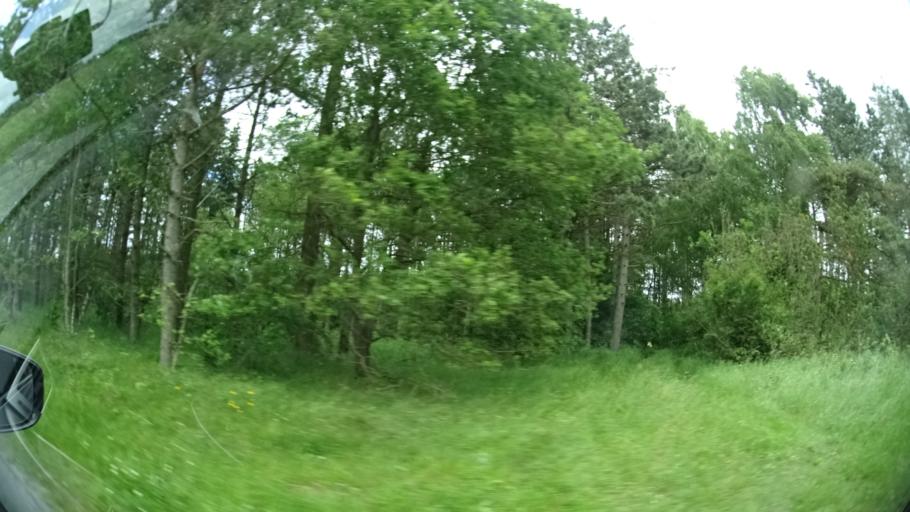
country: DK
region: Central Jutland
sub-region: Norddjurs Kommune
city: Grenaa
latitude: 56.5078
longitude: 10.7326
